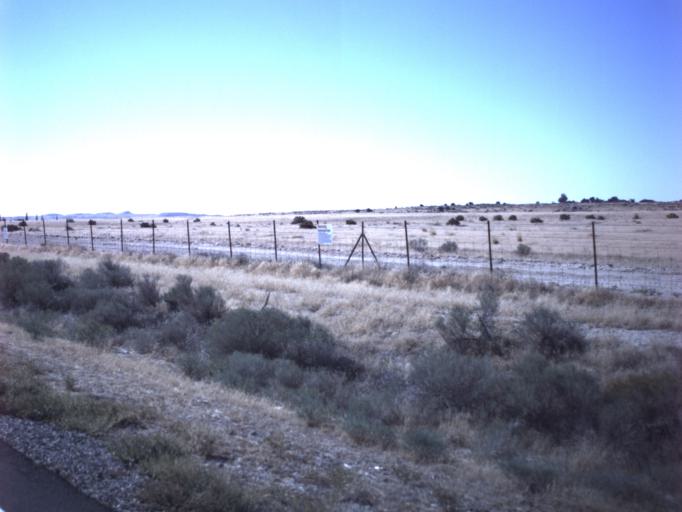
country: US
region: Utah
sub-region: Tooele County
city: Grantsville
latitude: 40.2392
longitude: -112.7232
